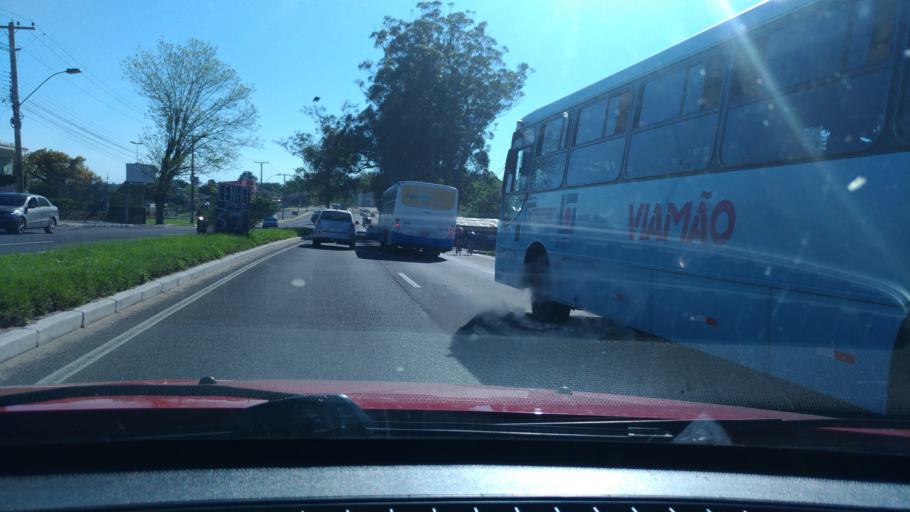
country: BR
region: Rio Grande do Sul
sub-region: Viamao
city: Viamao
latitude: -30.0943
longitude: -51.0786
